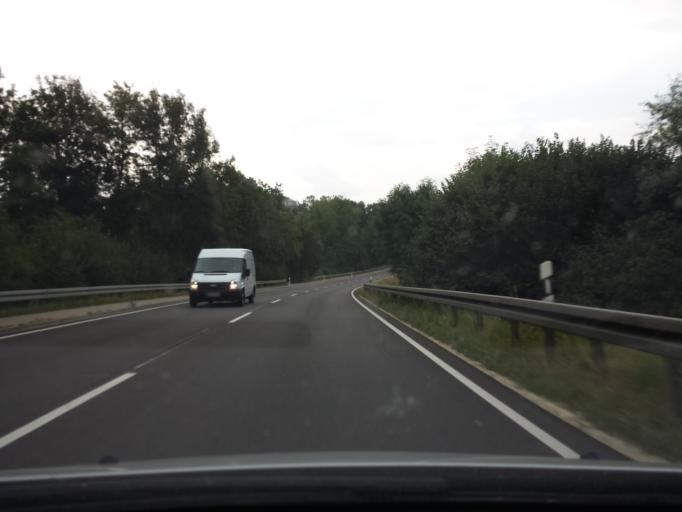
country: DE
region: Bavaria
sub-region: Swabia
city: Leipheim
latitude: 48.4336
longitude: 10.1779
